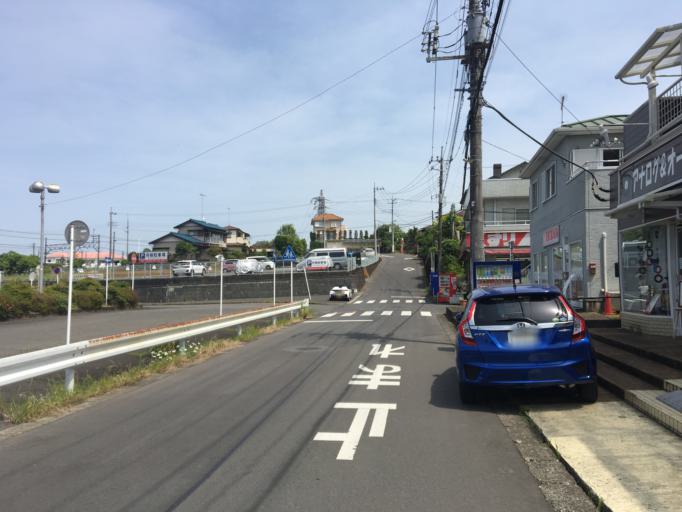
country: JP
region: Saitama
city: Hanno
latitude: 35.8812
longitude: 139.3039
